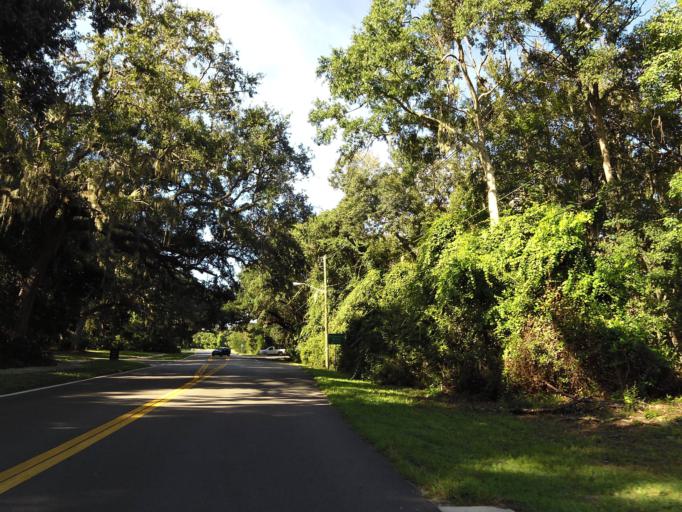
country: US
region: Florida
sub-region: Nassau County
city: Fernandina Beach
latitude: 30.5991
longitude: -81.4596
